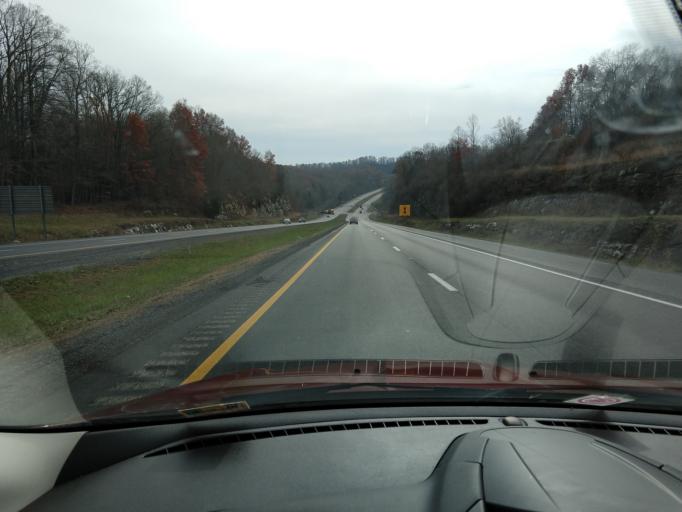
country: US
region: West Virginia
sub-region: Nicholas County
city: Summersville
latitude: 38.2802
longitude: -80.8348
